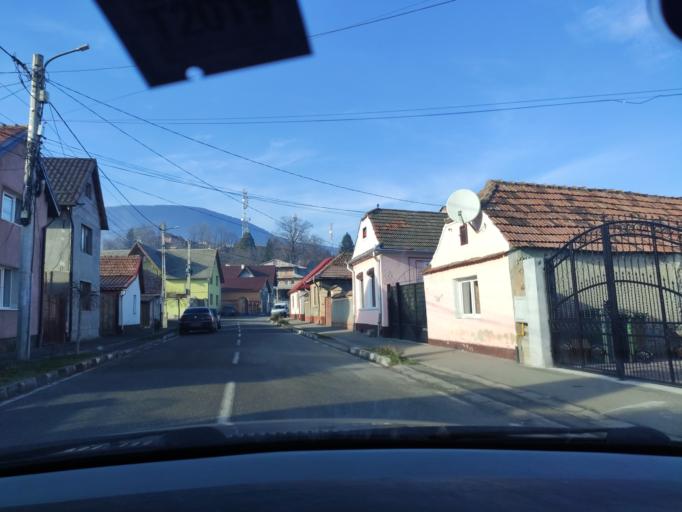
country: RO
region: Brasov
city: Codlea
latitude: 45.6931
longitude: 25.4439
